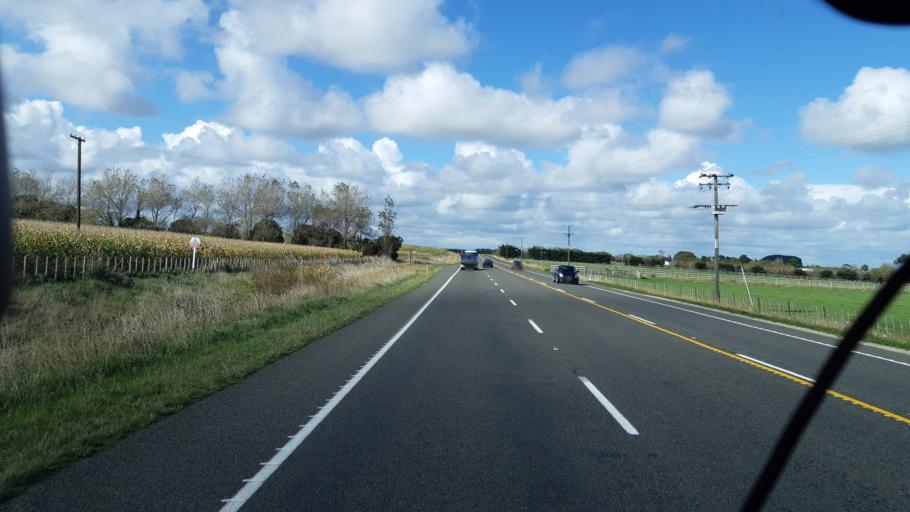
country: NZ
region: Manawatu-Wanganui
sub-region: Wanganui District
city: Wanganui
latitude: -39.9802
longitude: 175.1427
